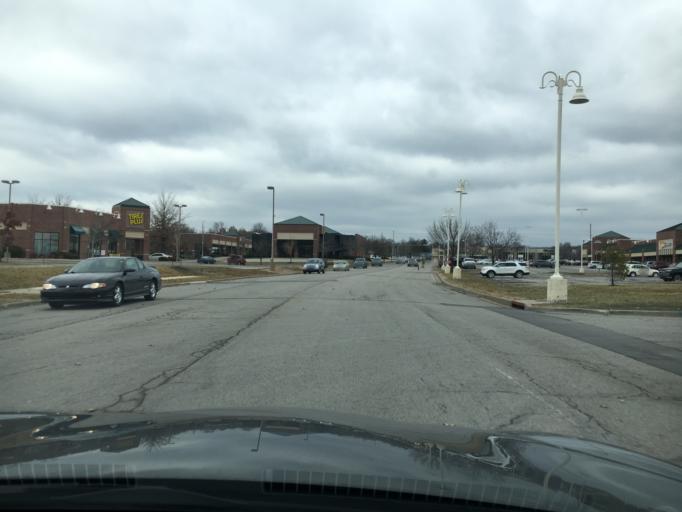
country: US
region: Kansas
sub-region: Johnson County
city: Overland Park
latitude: 38.9105
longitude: -94.6746
